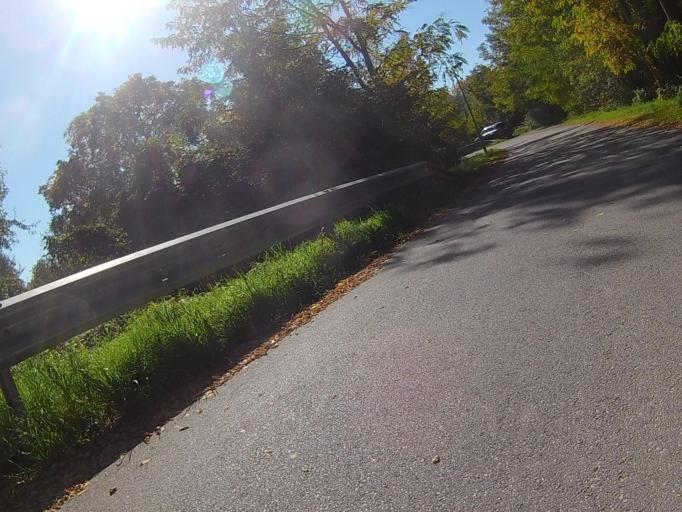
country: SI
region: Maribor
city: Maribor
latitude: 46.5574
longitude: 15.6842
